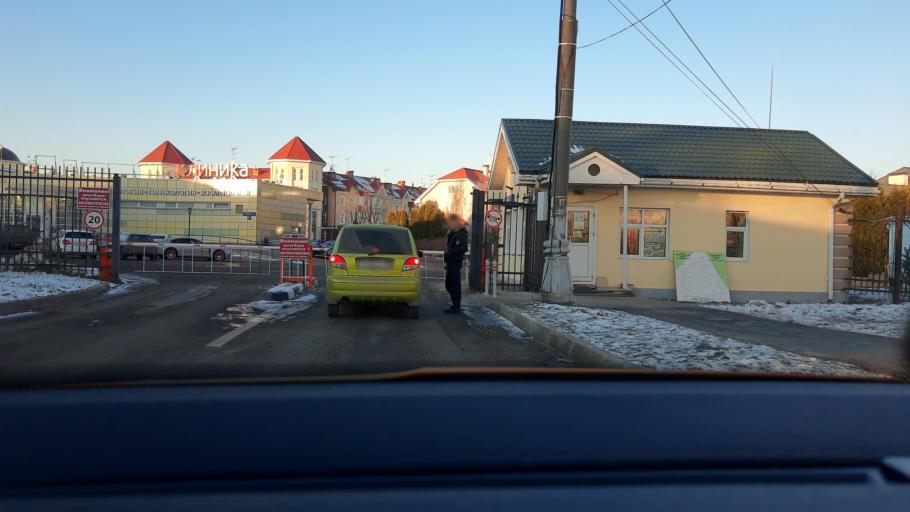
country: RU
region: Moskovskaya
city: Novopodrezkovo
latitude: 55.9001
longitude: 37.3760
